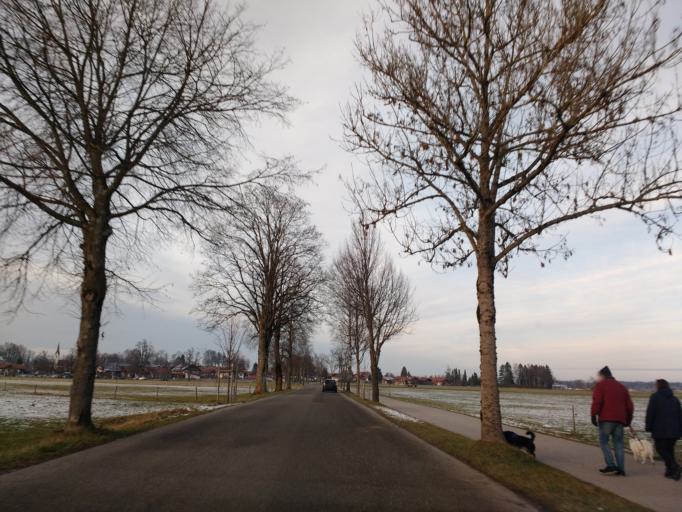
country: DE
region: Bavaria
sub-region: Swabia
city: Schwangau
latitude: 47.5710
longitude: 10.7372
